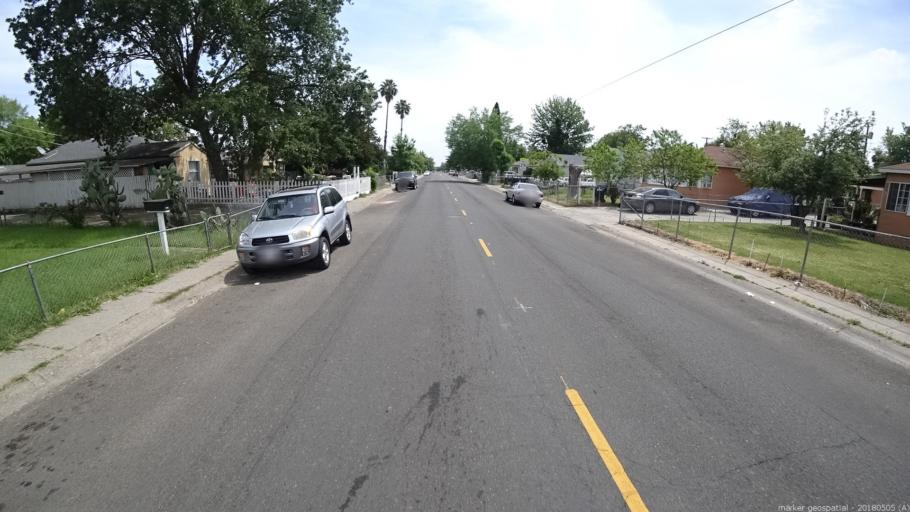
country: US
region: California
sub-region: Sacramento County
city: Arden-Arcade
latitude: 38.6328
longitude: -121.4273
